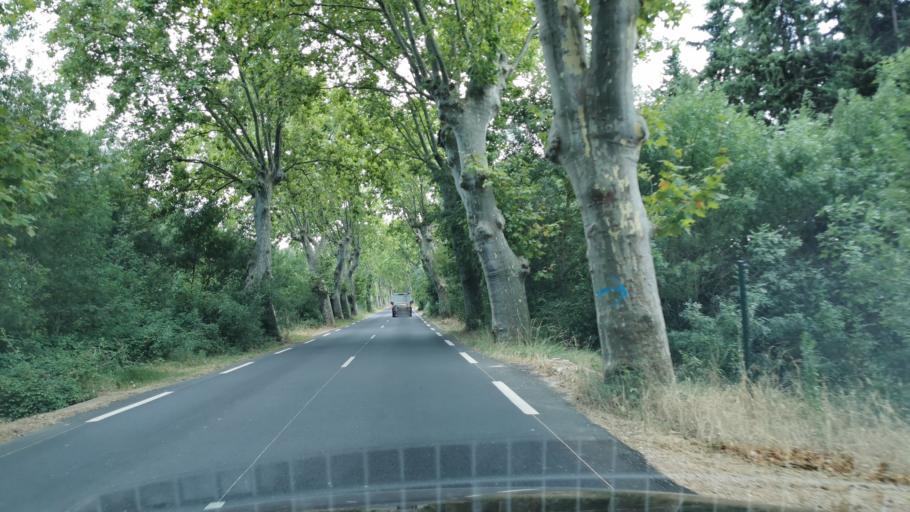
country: FR
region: Languedoc-Roussillon
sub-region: Departement de l'Herault
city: Capestang
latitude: 43.3229
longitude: 3.0362
